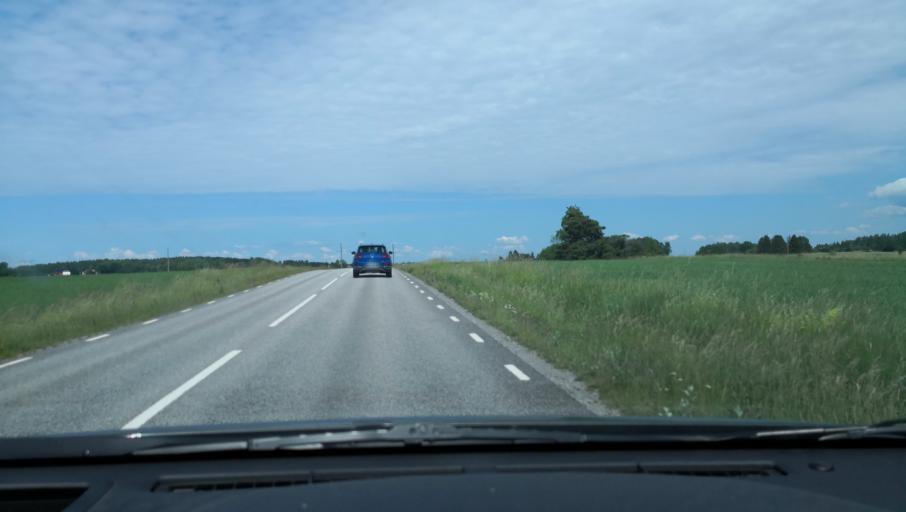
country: SE
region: Stockholm
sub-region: Sigtuna Kommun
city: Sigtuna
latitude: 59.6665
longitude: 17.6924
